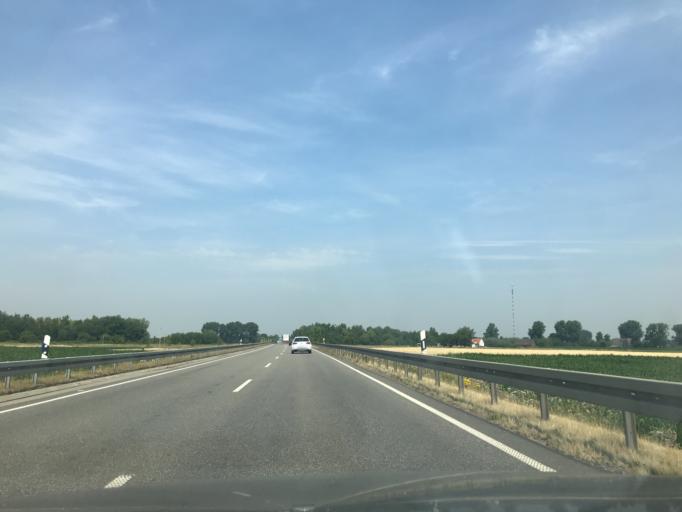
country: DE
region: North Rhine-Westphalia
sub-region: Regierungsbezirk Dusseldorf
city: Alpen
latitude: 51.6232
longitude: 6.5633
